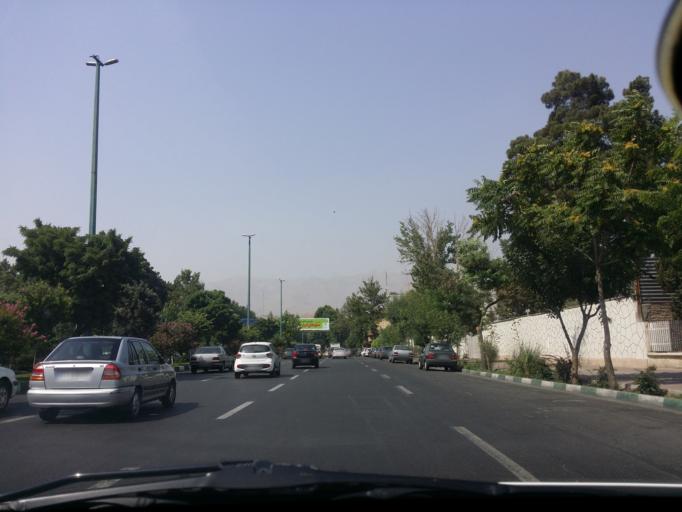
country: IR
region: Alborz
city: Karaj
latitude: 35.8056
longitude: 51.0027
